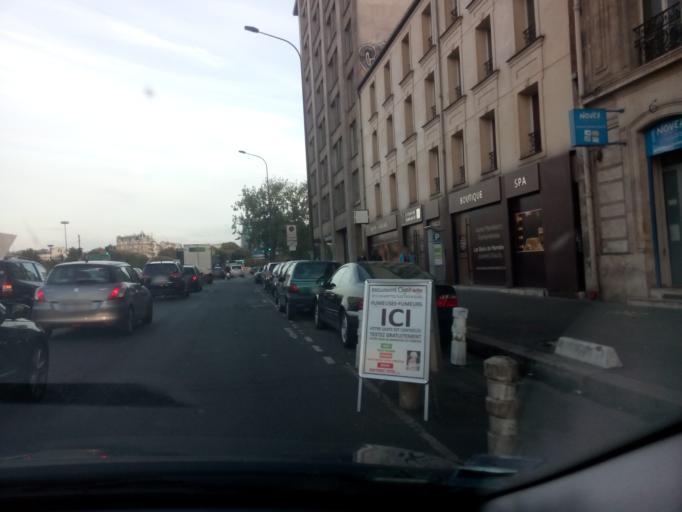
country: FR
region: Ile-de-France
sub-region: Departement des Hauts-de-Seine
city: Neuilly-sur-Seine
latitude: 48.8787
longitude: 2.2787
